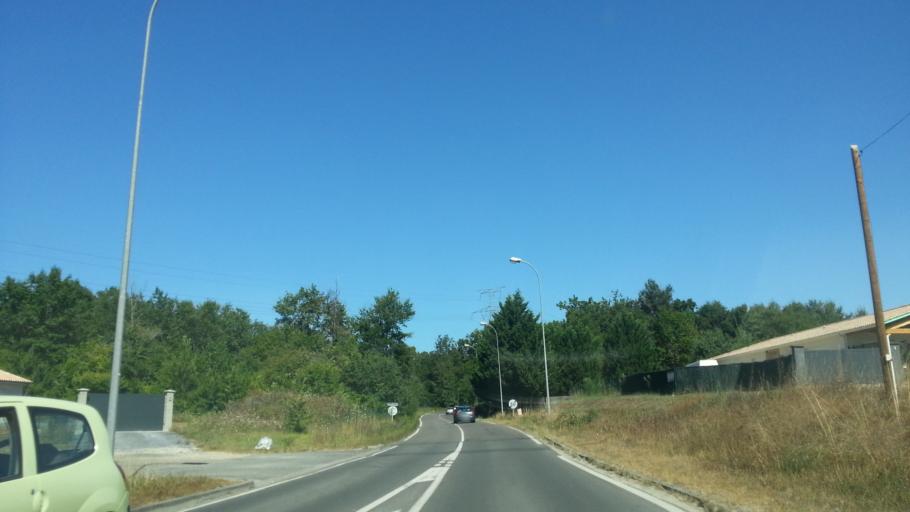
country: FR
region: Aquitaine
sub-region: Departement de la Gironde
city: Saint-Selve
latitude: 44.6753
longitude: -0.4957
